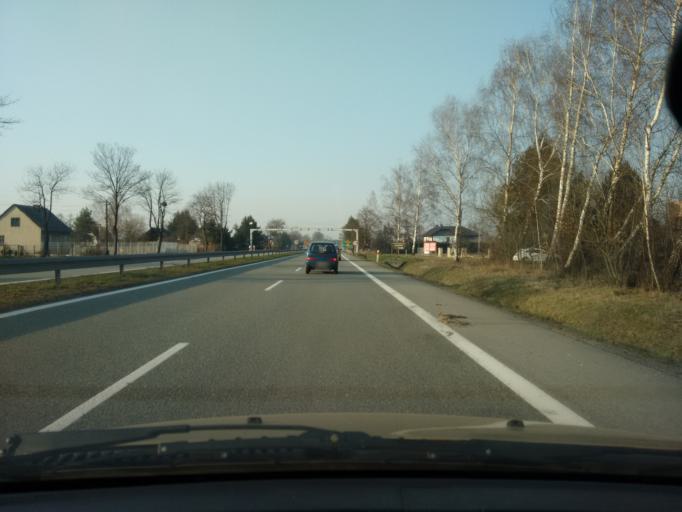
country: PL
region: Silesian Voivodeship
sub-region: Powiat cieszynski
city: Zbytkow
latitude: 49.9141
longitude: 18.7353
